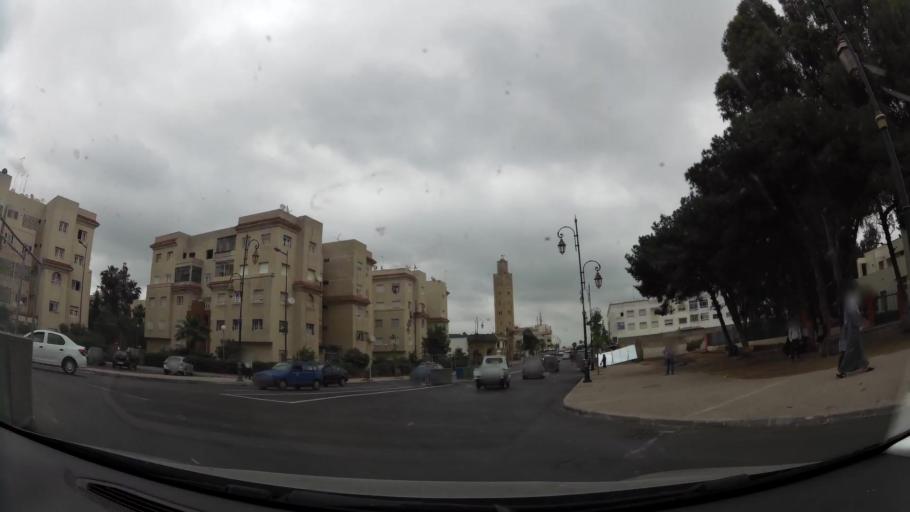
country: MA
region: Rabat-Sale-Zemmour-Zaer
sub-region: Rabat
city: Rabat
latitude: 33.9763
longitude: -6.8193
